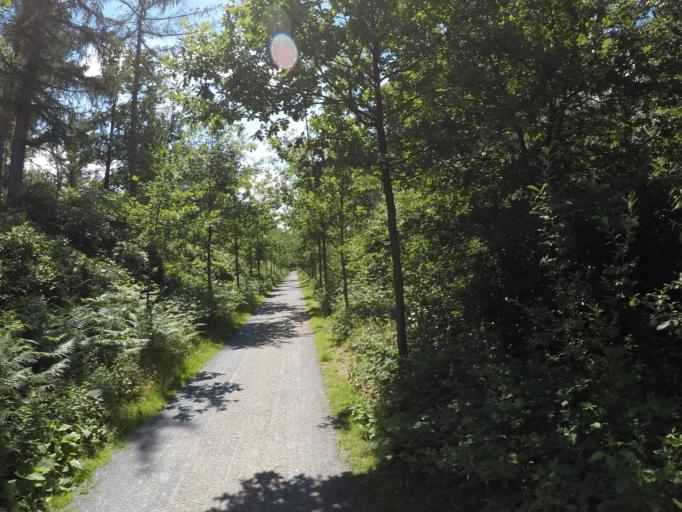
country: BE
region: Flanders
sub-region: Provincie Antwerpen
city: Vosselaar
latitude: 51.2914
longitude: 4.8874
